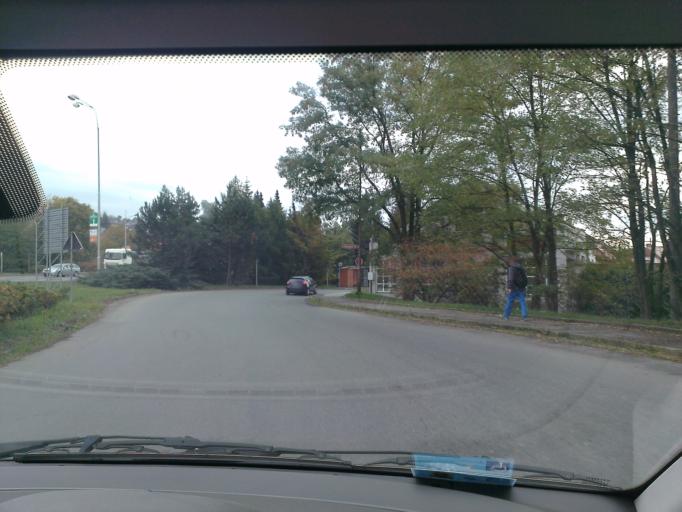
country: CZ
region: Zlin
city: Valasske Mezirici
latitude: 49.4836
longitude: 17.9656
